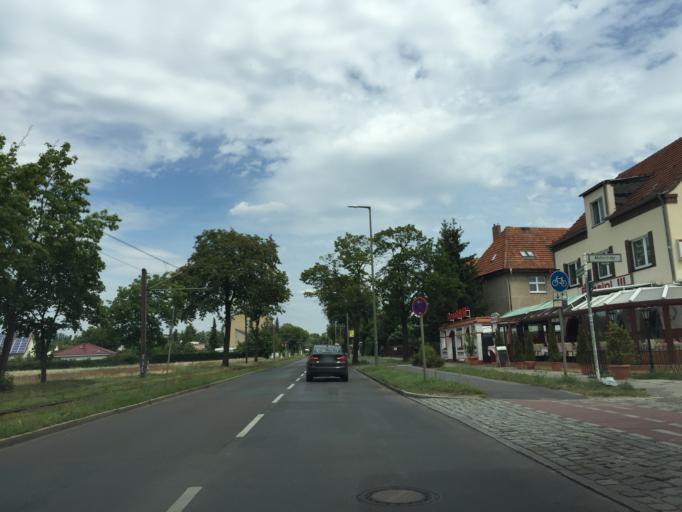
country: DE
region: Berlin
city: Mahlsdorf
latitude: 52.4954
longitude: 13.6108
